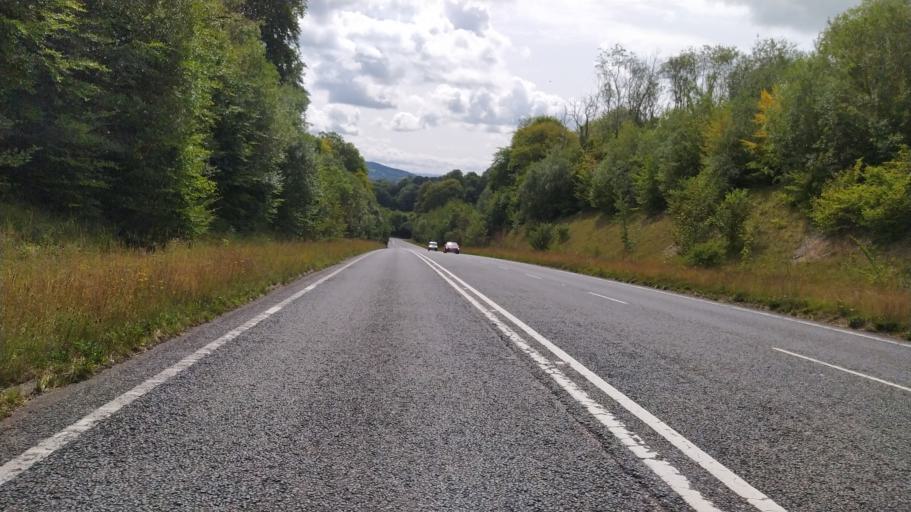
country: GB
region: England
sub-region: Wiltshire
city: Hindon
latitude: 51.0815
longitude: -2.1664
